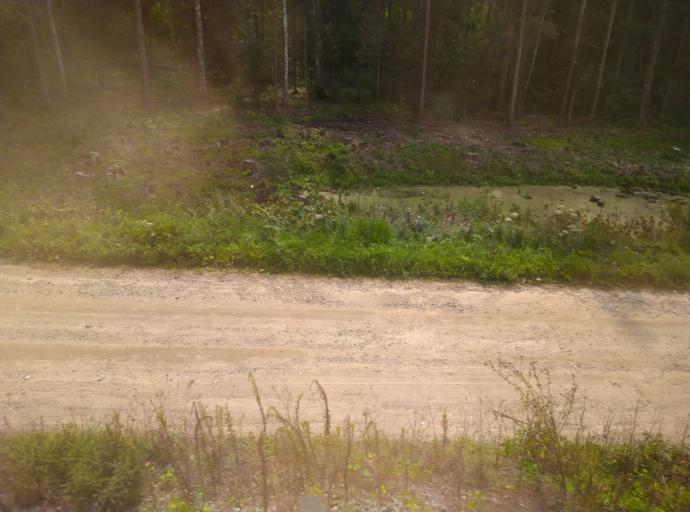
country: RU
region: Jaroslavl
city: Burmakino
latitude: 57.4364
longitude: 40.3435
